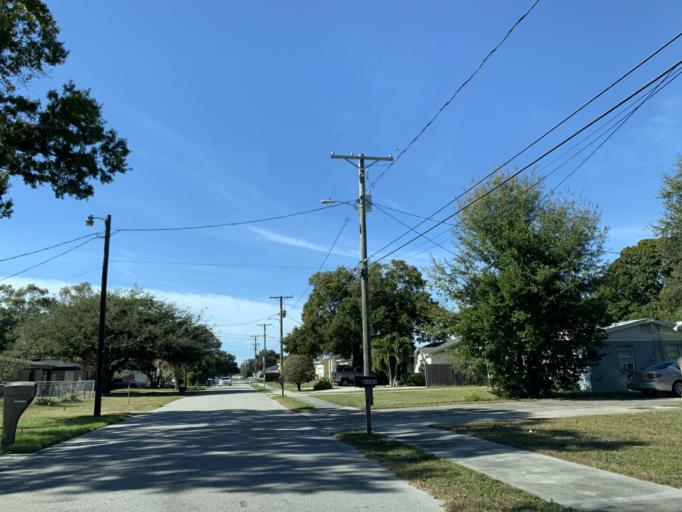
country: US
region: Florida
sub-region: Hillsborough County
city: Tampa
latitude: 27.8884
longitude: -82.5046
